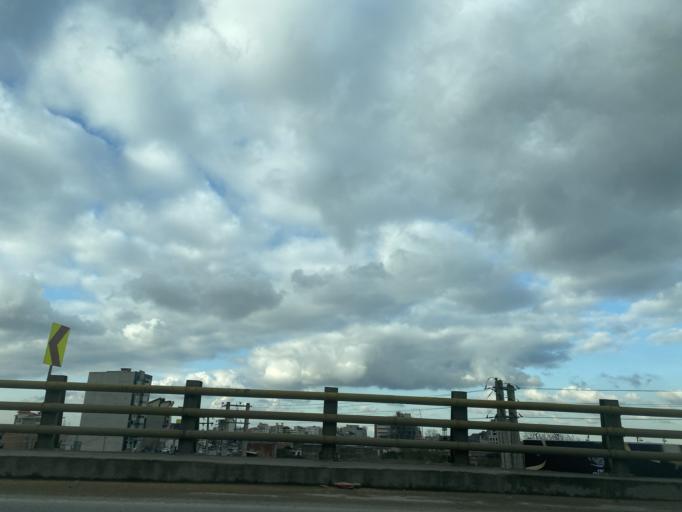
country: IR
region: Mazandaran
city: Amol
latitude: 36.4333
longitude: 52.3485
